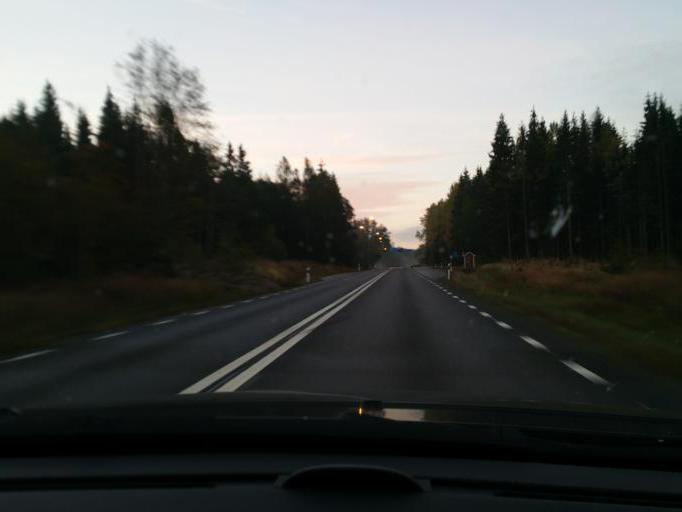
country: SE
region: Kronoberg
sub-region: Vaxjo Kommun
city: Lammhult
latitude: 57.0926
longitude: 14.6399
